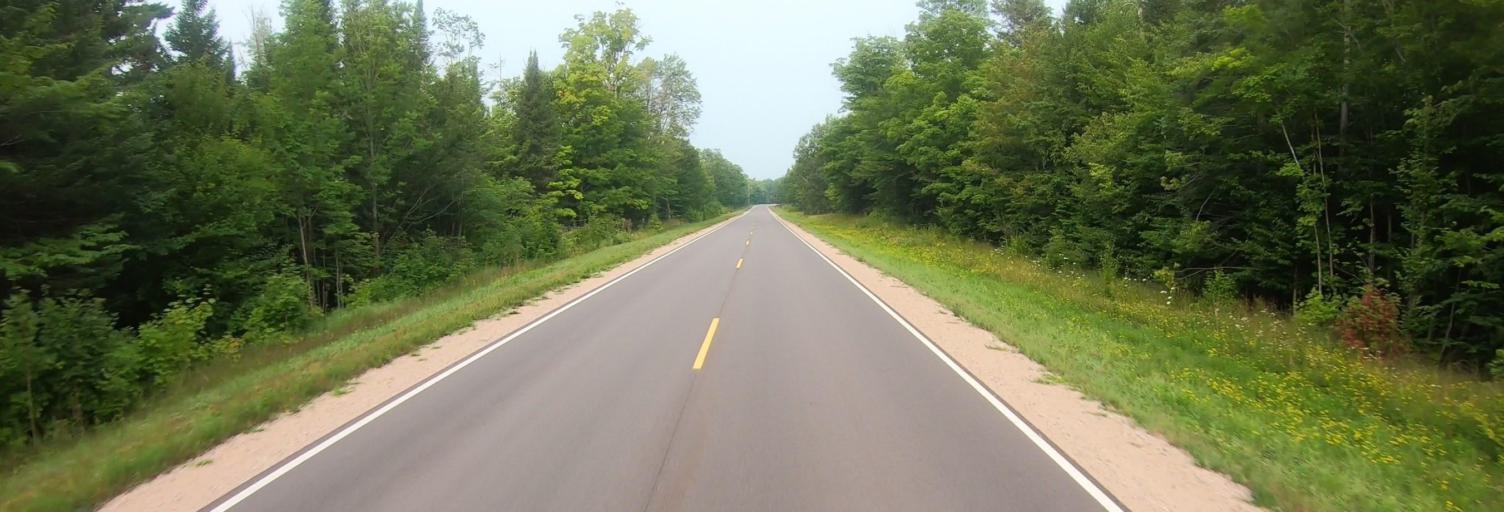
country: US
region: Michigan
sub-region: Luce County
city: Newberry
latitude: 46.4805
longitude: -85.0688
